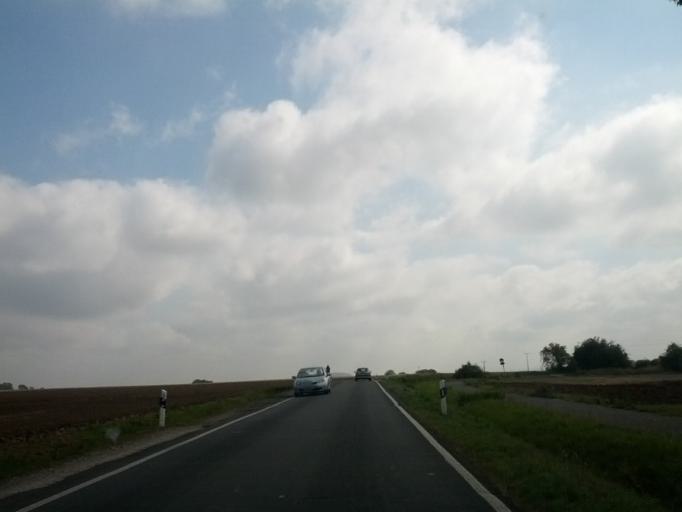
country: DE
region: Thuringia
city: Schwabhausen
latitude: 50.9158
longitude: 10.7434
